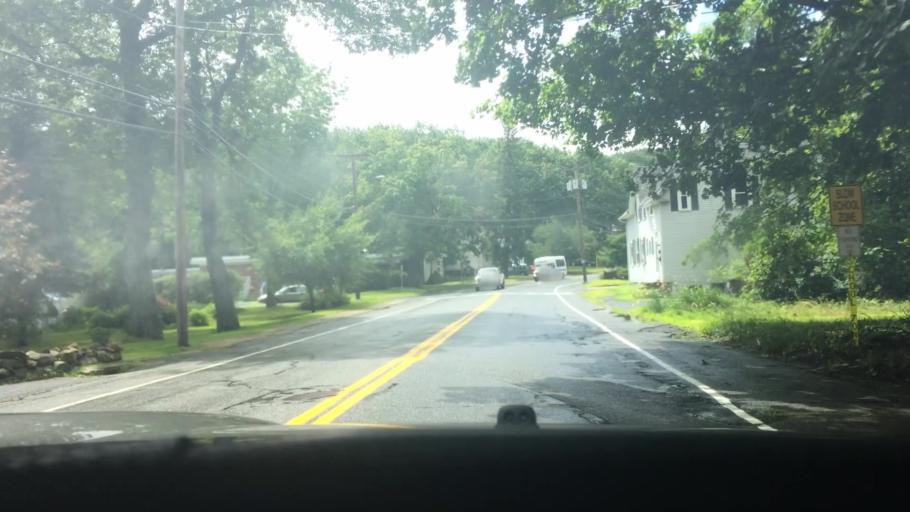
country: US
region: Massachusetts
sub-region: Worcester County
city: Gardner
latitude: 42.5845
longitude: -71.9856
